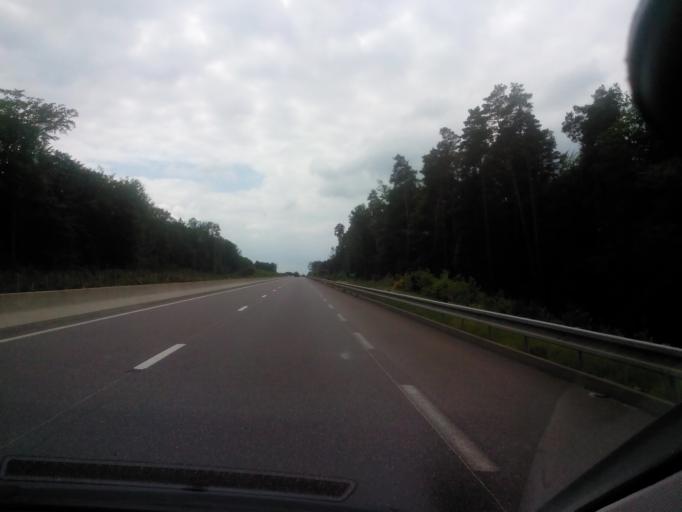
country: FR
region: Lorraine
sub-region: Departement de la Moselle
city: Carling
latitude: 49.1952
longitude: 6.7184
